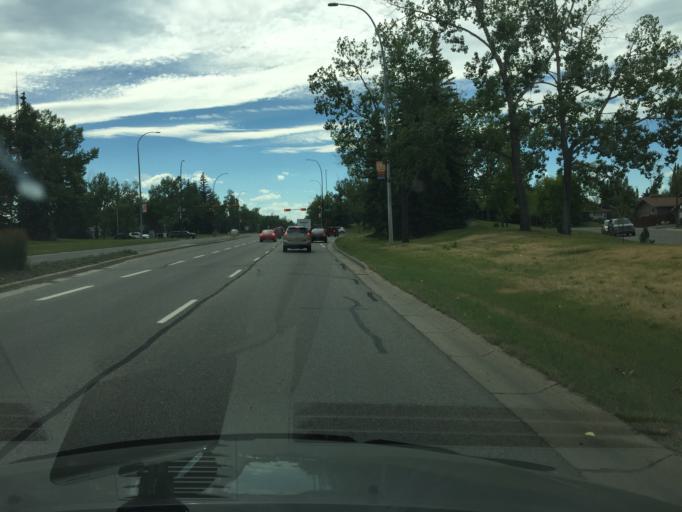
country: CA
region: Alberta
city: Calgary
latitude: 50.9306
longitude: -114.0366
